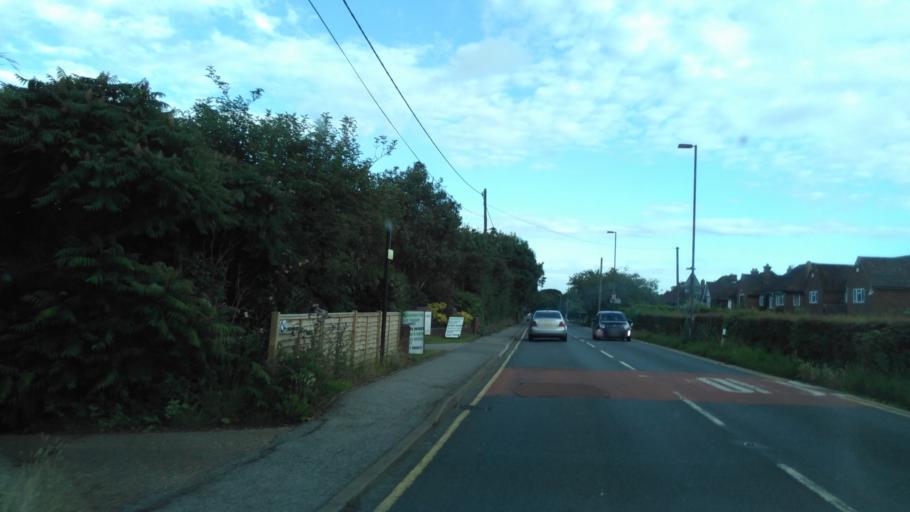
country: GB
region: England
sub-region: Kent
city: Blean
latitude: 51.2977
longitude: 1.0512
